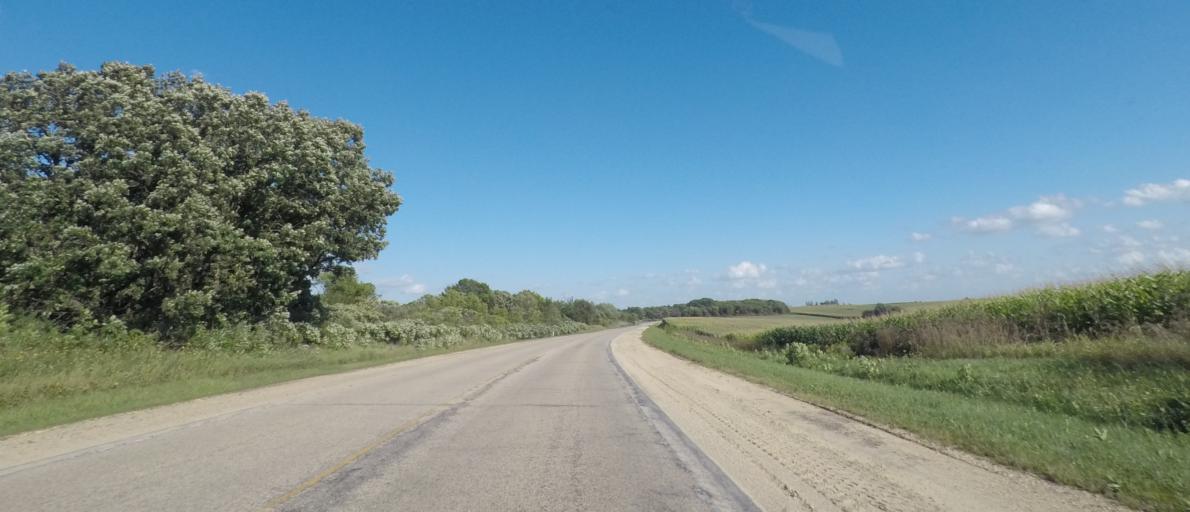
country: US
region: Wisconsin
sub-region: Iowa County
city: Dodgeville
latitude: 42.9790
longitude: -90.0577
